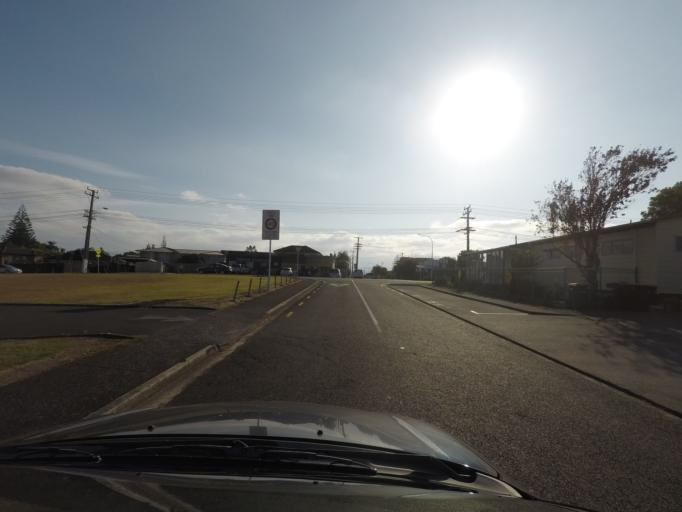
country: NZ
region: Auckland
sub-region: Auckland
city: Rosebank
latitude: -36.8595
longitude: 174.6446
